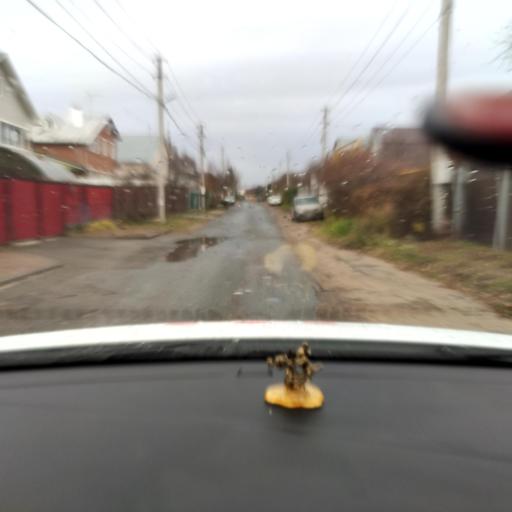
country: RU
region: Tatarstan
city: Vysokaya Gora
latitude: 55.8438
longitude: 49.2390
